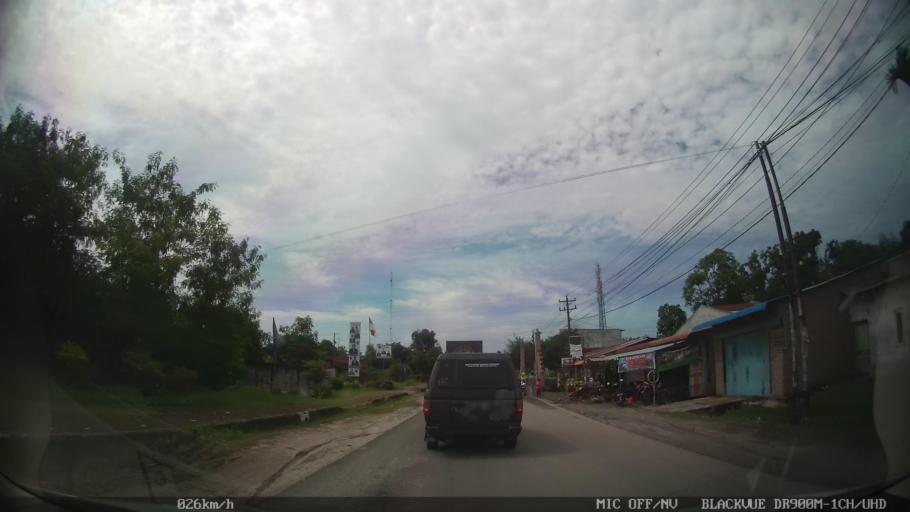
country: ID
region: North Sumatra
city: Percut
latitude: 3.6021
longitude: 98.8075
